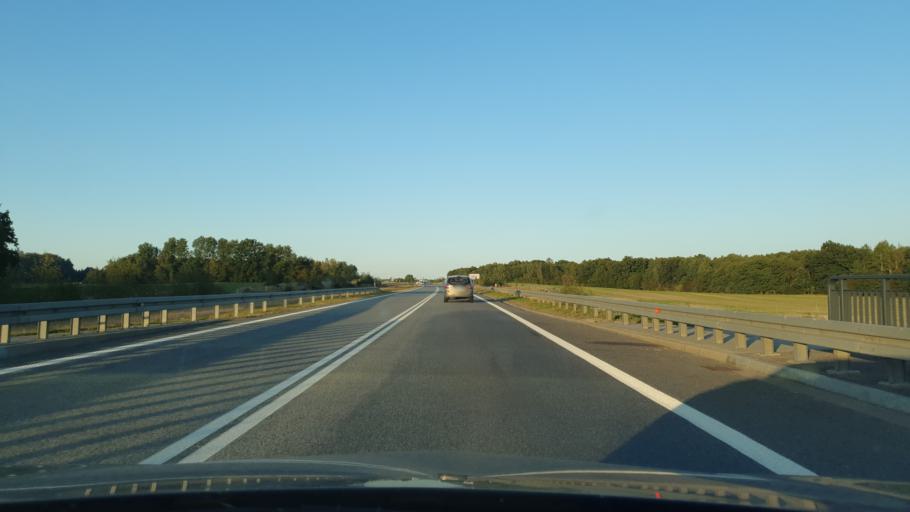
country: PL
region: Pomeranian Voivodeship
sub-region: Slupsk
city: Slupsk
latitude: 54.4605
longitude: 17.1045
